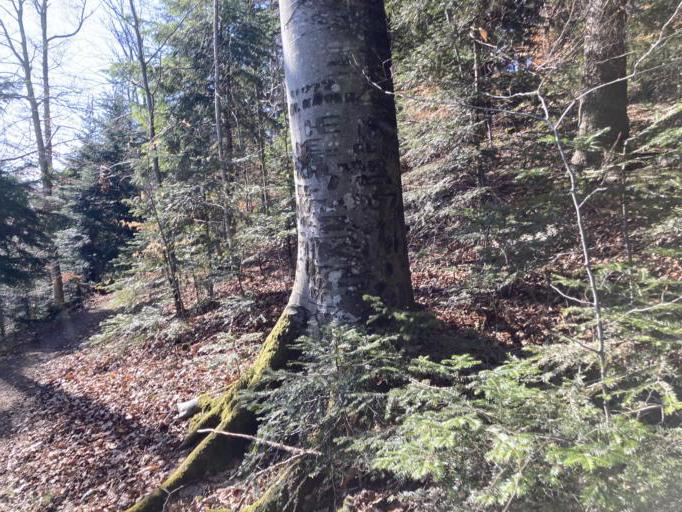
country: DE
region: Baden-Wuerttemberg
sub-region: Freiburg Region
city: Glottertal
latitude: 48.0603
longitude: 7.9636
